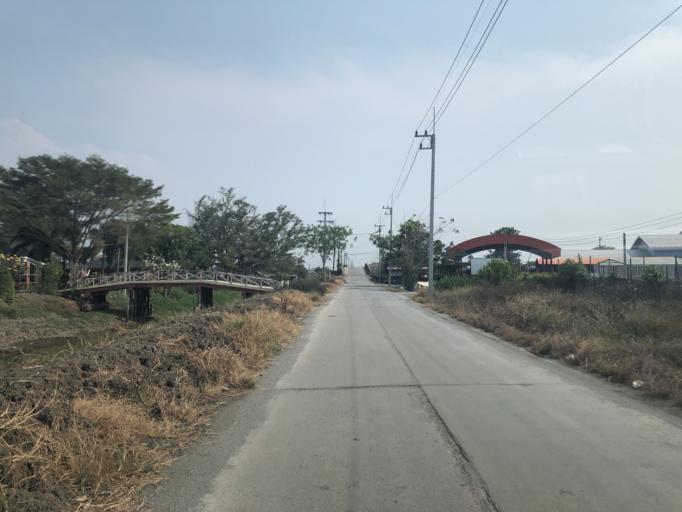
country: TH
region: Samut Prakan
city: Bang Bo
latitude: 13.5332
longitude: 100.9039
